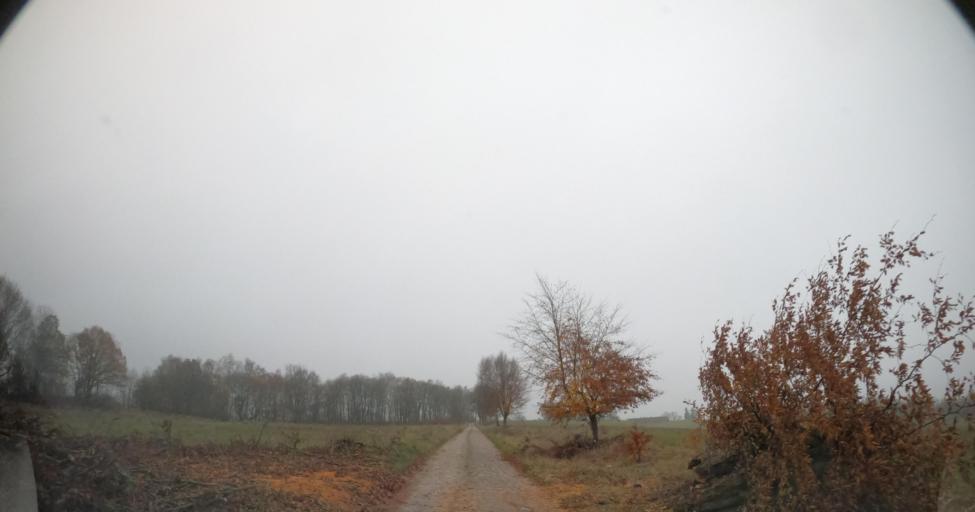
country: PL
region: West Pomeranian Voivodeship
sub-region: Powiat drawski
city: Drawsko Pomorskie
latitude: 53.5458
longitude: 15.7275
